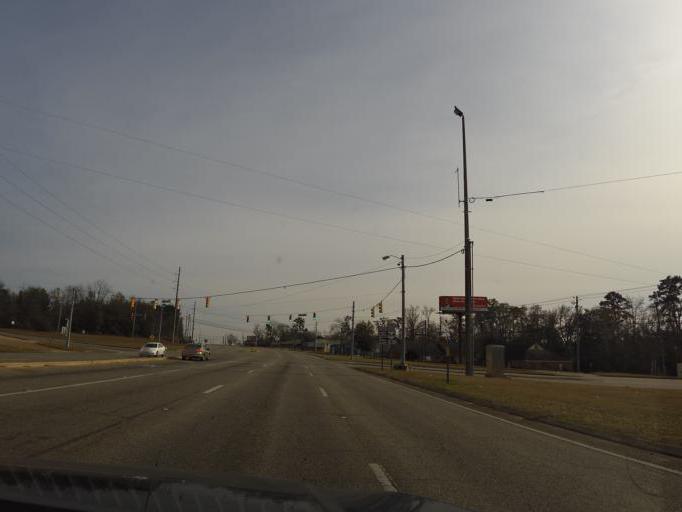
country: US
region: Alabama
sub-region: Houston County
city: Dothan
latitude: 31.2209
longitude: -85.3708
